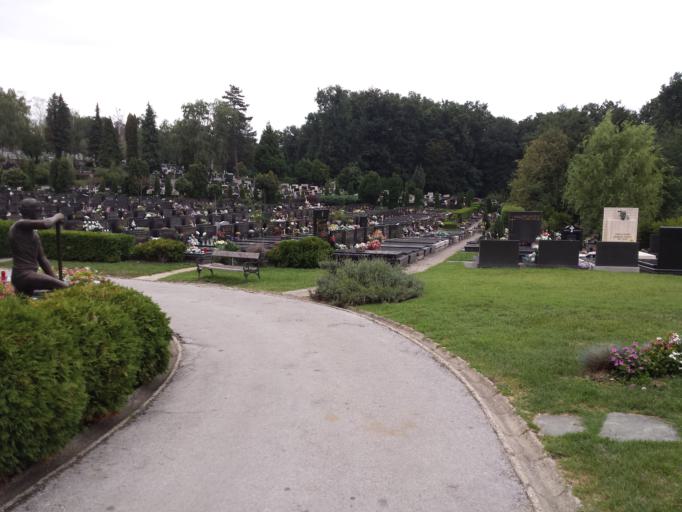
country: HR
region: Grad Zagreb
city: Zagreb
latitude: 45.8385
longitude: 15.9860
